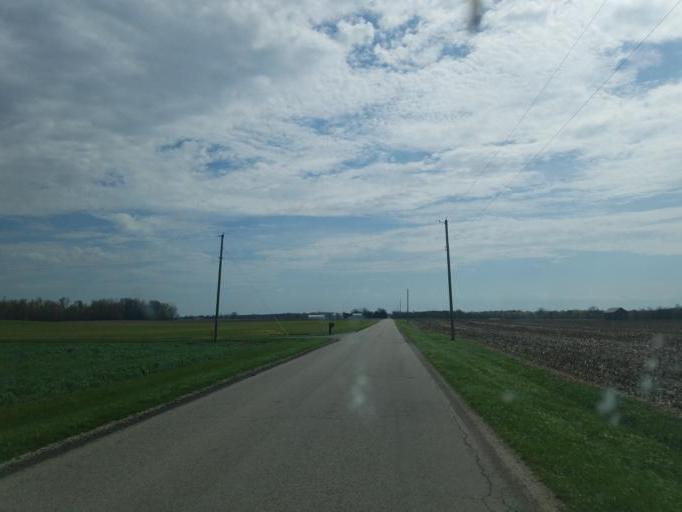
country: US
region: Ohio
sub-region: Crawford County
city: Bucyrus
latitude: 40.7902
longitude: -83.0536
